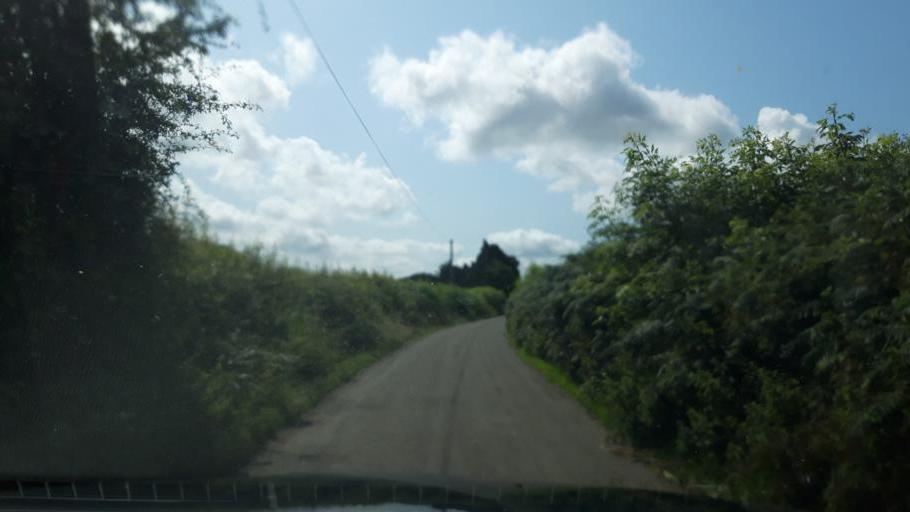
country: IE
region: Leinster
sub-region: Kilkenny
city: Graiguenamanagh
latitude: 52.5707
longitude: -6.9810
